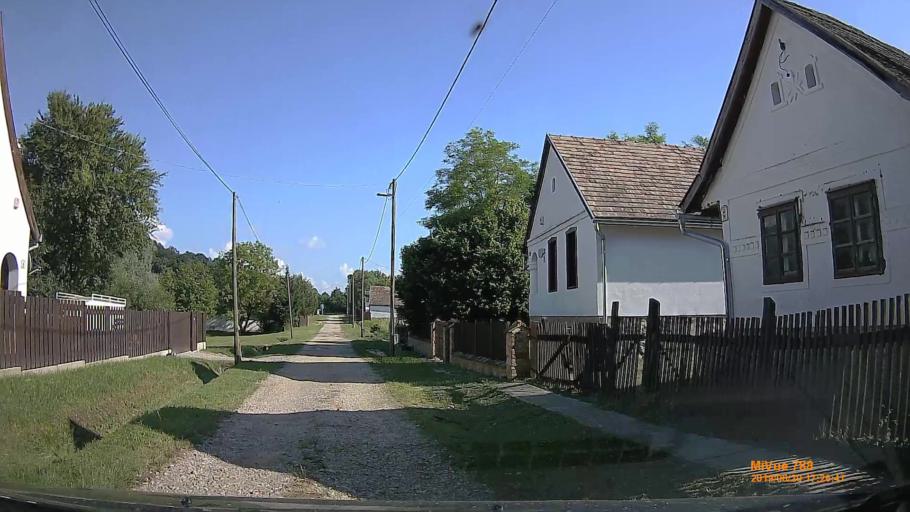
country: HU
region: Baranya
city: Buekkoesd
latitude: 46.1610
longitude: 18.0101
